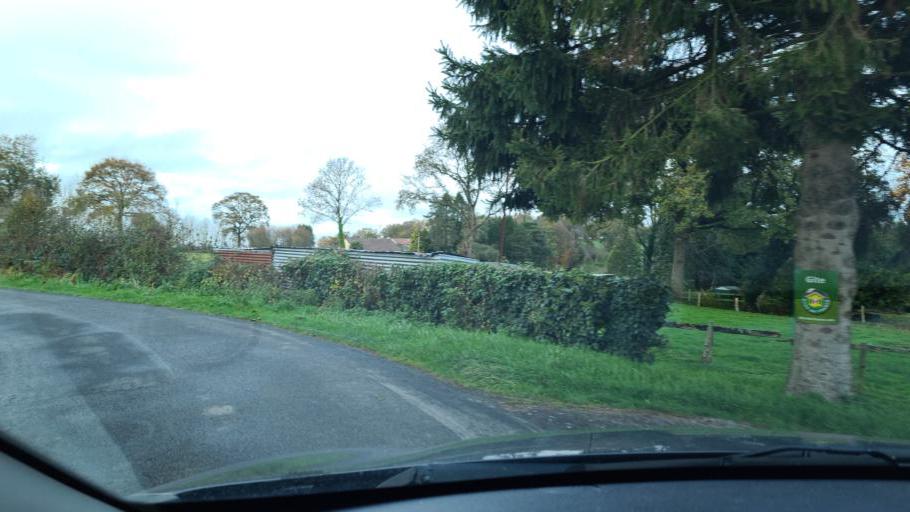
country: FR
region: Lower Normandy
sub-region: Departement de la Manche
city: La Haye-Pesnel
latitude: 48.7845
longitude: -1.3998
